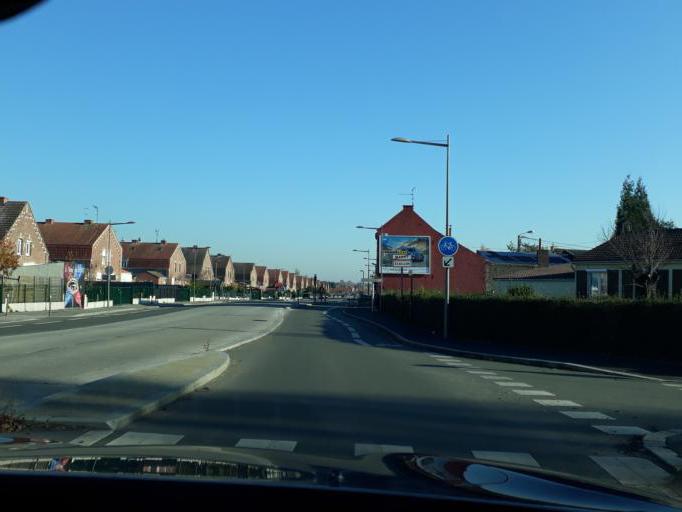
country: FR
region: Nord-Pas-de-Calais
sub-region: Departement du Nord
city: Masny
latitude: 50.3366
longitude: 3.2039
